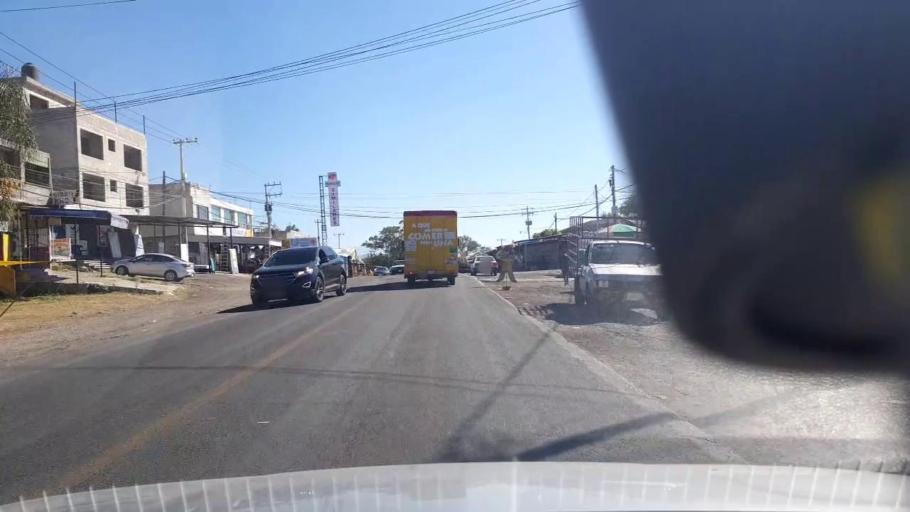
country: MX
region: Morelos
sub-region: Cuernavaca
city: Lomas de Ahuatepec
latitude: 18.9695
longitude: -99.2184
